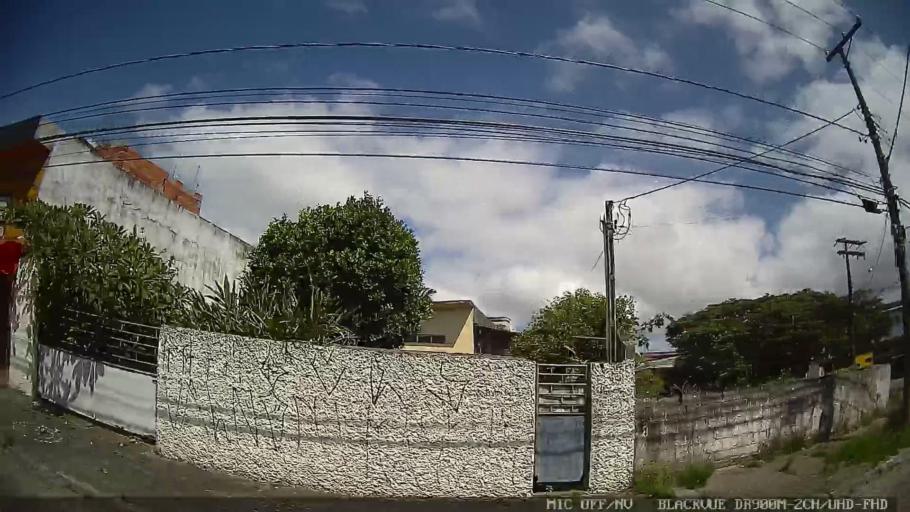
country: BR
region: Sao Paulo
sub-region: Peruibe
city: Peruibe
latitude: -24.3167
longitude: -47.0086
